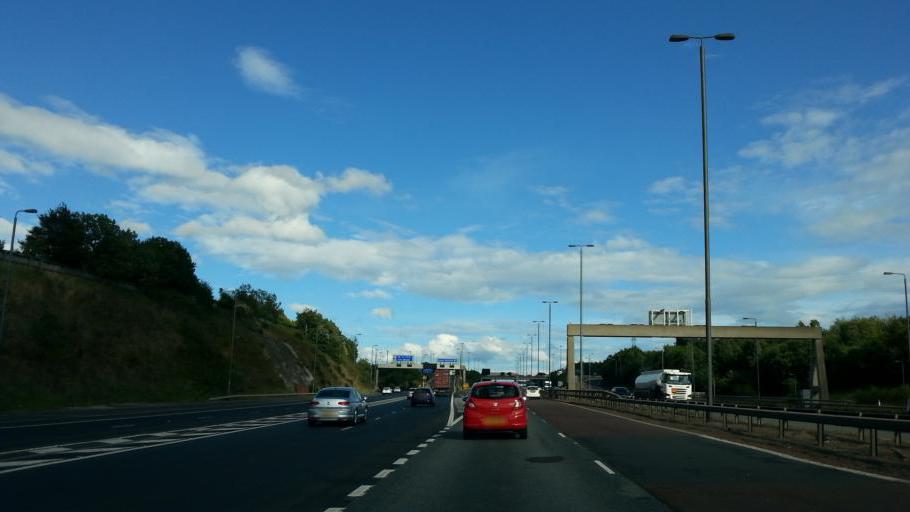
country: GB
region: England
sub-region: City and Borough of Leeds
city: Lofthouse
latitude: 53.7328
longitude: -1.5205
